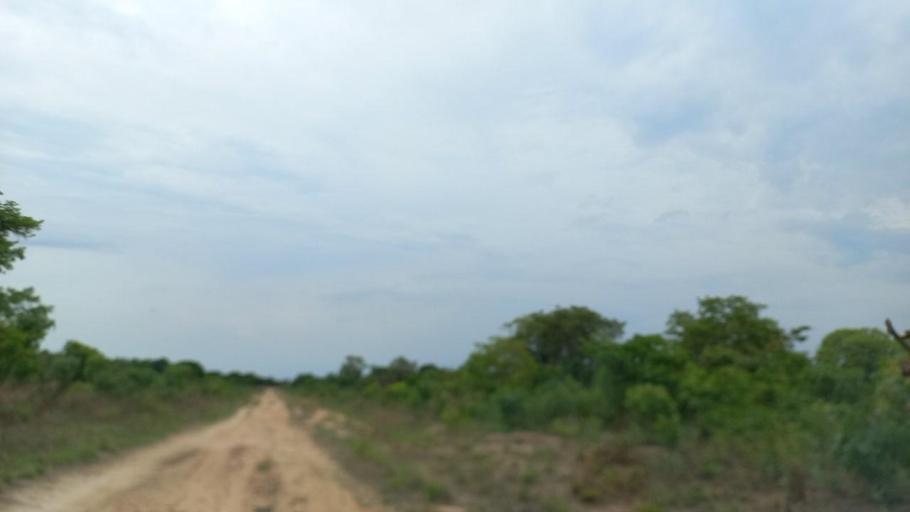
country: ZM
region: North-Western
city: Kalengwa
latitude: -13.6383
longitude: 24.9801
